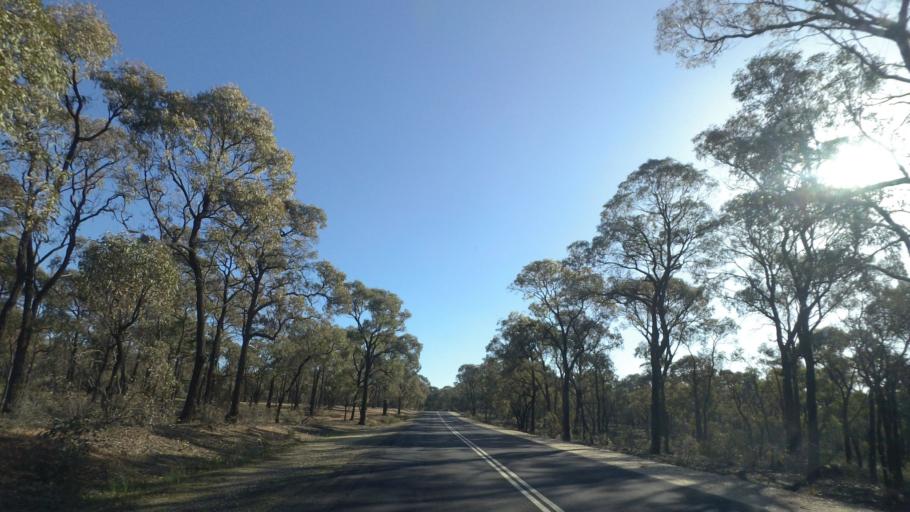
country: AU
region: Victoria
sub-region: Greater Bendigo
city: Kangaroo Flat
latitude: -36.8227
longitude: 144.2696
